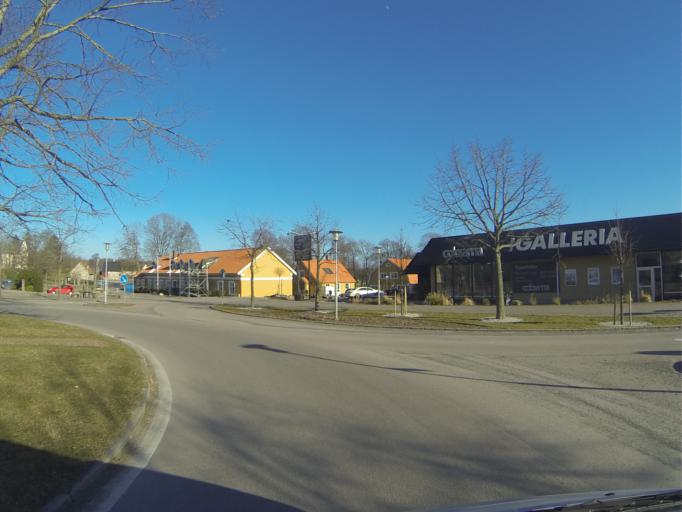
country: SE
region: Skane
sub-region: Hoors Kommun
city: Hoeoer
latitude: 55.9304
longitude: 13.5475
